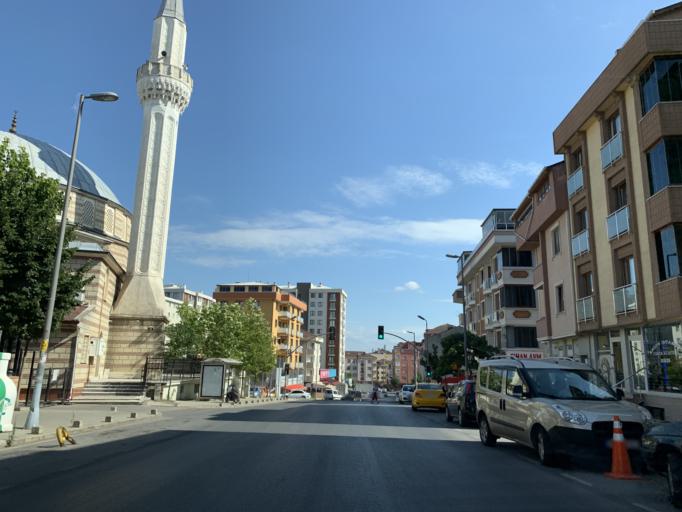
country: TR
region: Istanbul
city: Pendik
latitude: 40.8881
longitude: 29.2727
